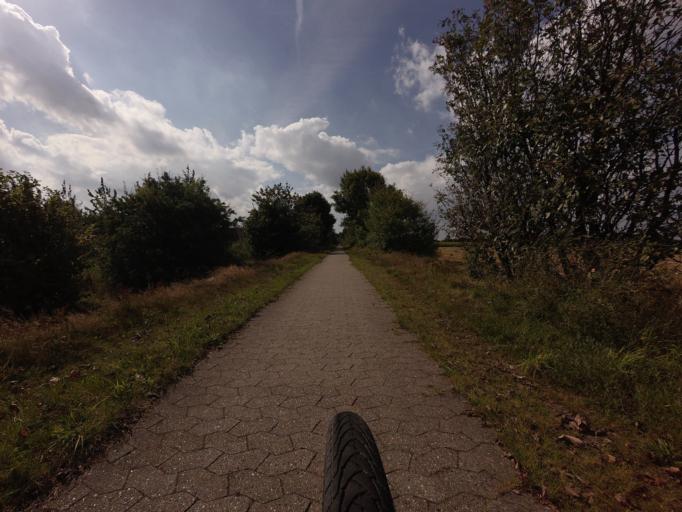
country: DK
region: Central Jutland
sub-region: Viborg Kommune
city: Karup
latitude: 56.3338
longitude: 9.2385
